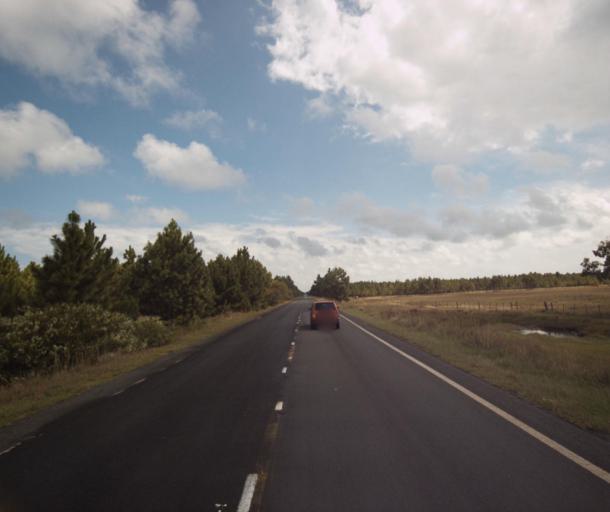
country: BR
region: Rio Grande do Sul
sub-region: Tapes
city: Tapes
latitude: -31.4129
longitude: -51.1710
